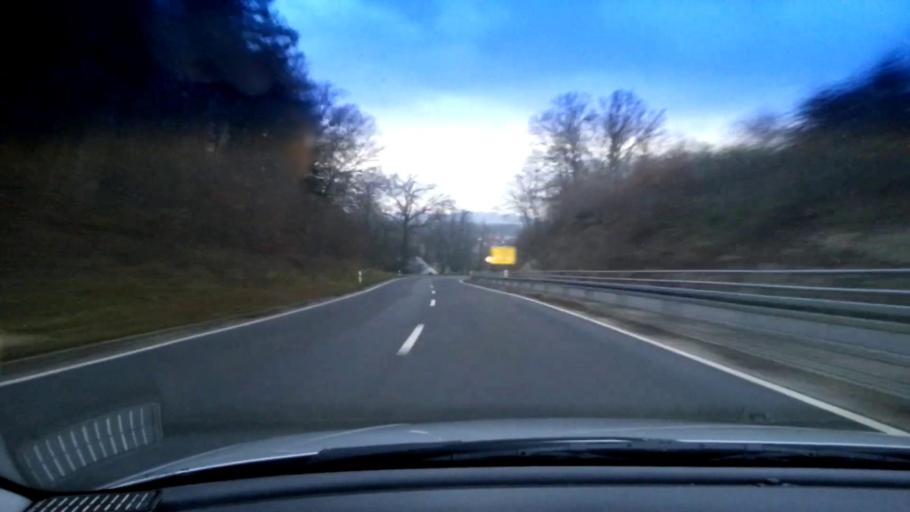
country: DE
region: Bavaria
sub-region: Upper Franconia
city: Frensdorf
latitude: 49.8468
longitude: 10.8779
